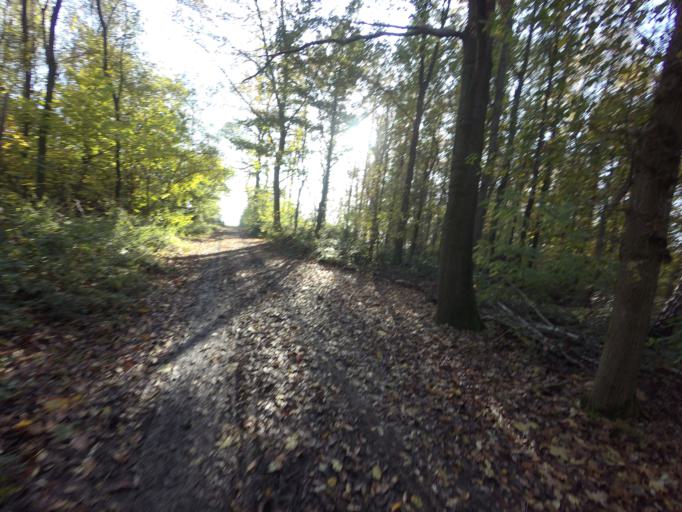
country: NL
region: Limburg
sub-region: Eijsden-Margraten
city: Margraten
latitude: 50.7863
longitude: 5.8705
